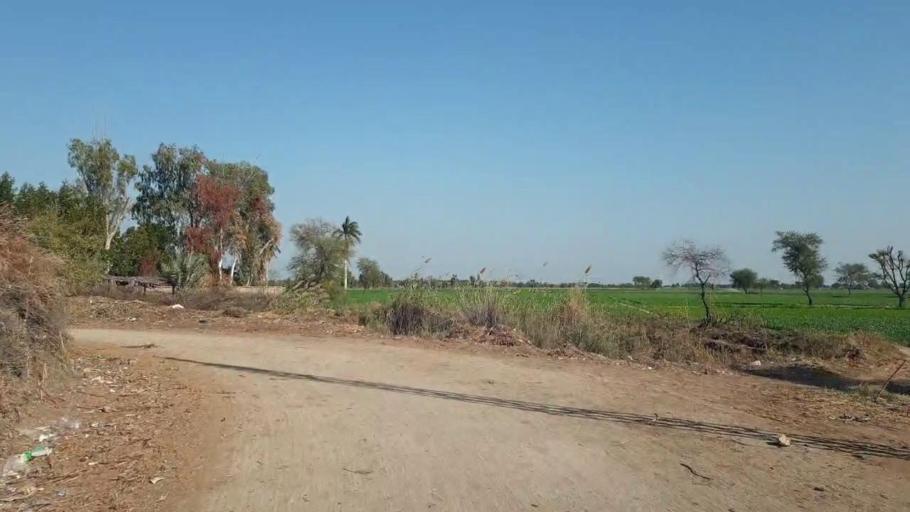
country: PK
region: Sindh
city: Shahdadpur
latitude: 25.9778
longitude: 68.6692
